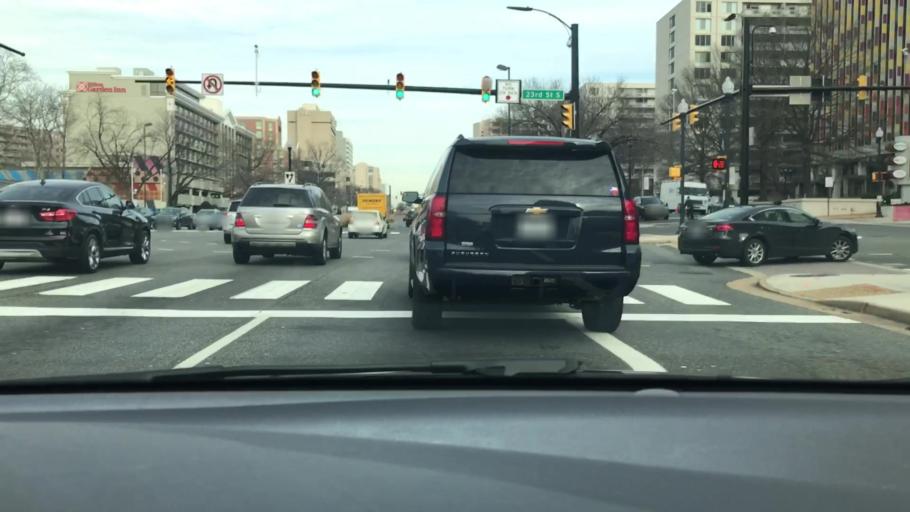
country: US
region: Washington, D.C.
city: Washington, D.C.
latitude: 38.8531
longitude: -77.0524
